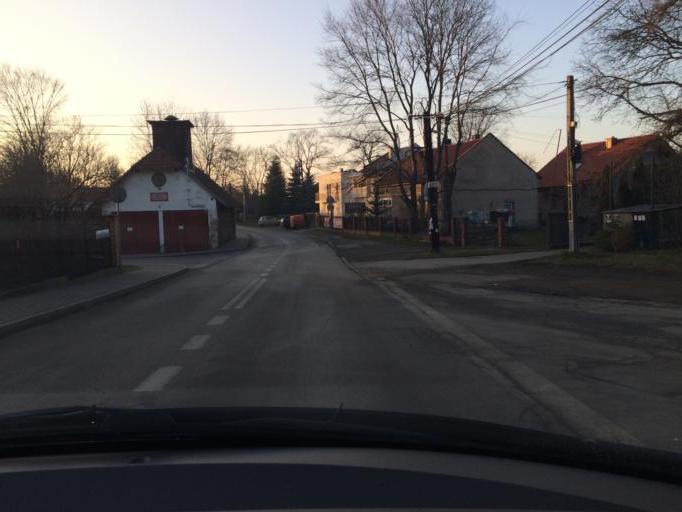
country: PL
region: Lesser Poland Voivodeship
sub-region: Powiat wielicki
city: Czarnochowice
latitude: 50.0161
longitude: 20.0381
